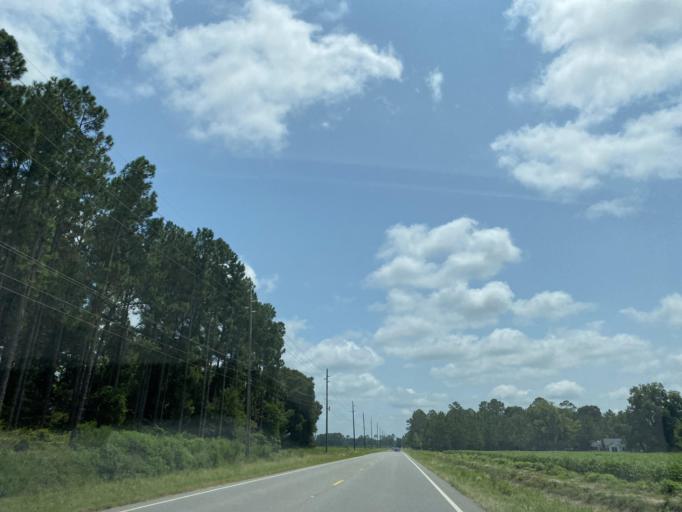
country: US
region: Georgia
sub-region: Jeff Davis County
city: Hazlehurst
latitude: 31.8294
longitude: -82.5743
